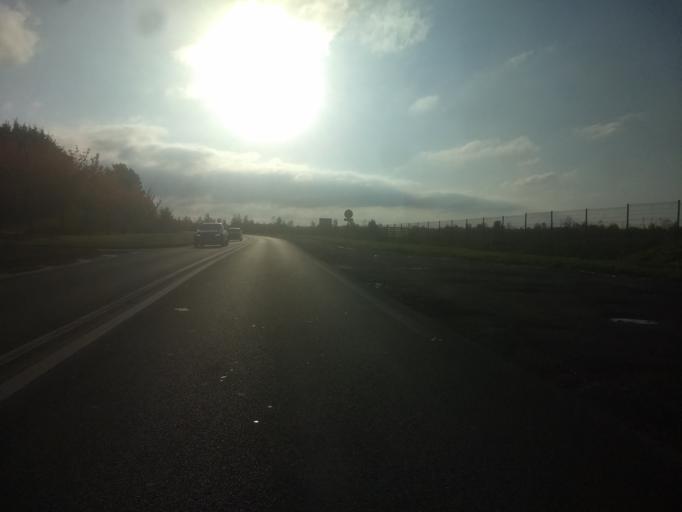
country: FR
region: Nord-Pas-de-Calais
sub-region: Departement du Pas-de-Calais
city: Tilloy-les-Mofflaines
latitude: 50.2778
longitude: 2.8124
